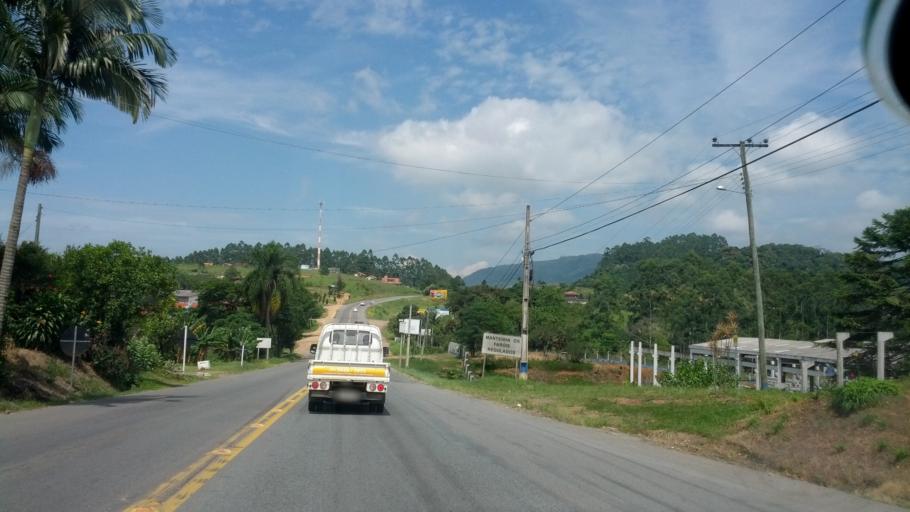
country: BR
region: Santa Catarina
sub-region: Ibirama
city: Ibirama
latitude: -27.1085
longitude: -49.5245
